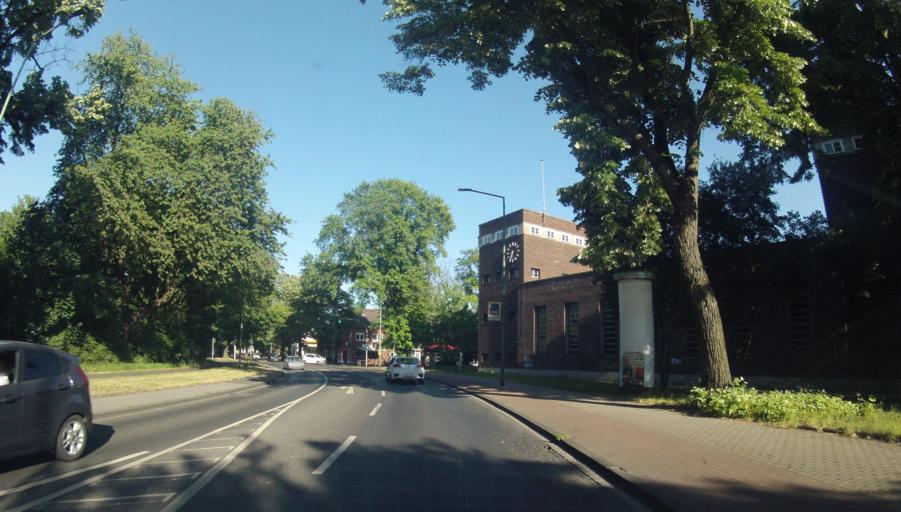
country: DE
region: North Rhine-Westphalia
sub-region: Regierungsbezirk Dusseldorf
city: Hochfeld
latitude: 51.4056
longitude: 6.7671
